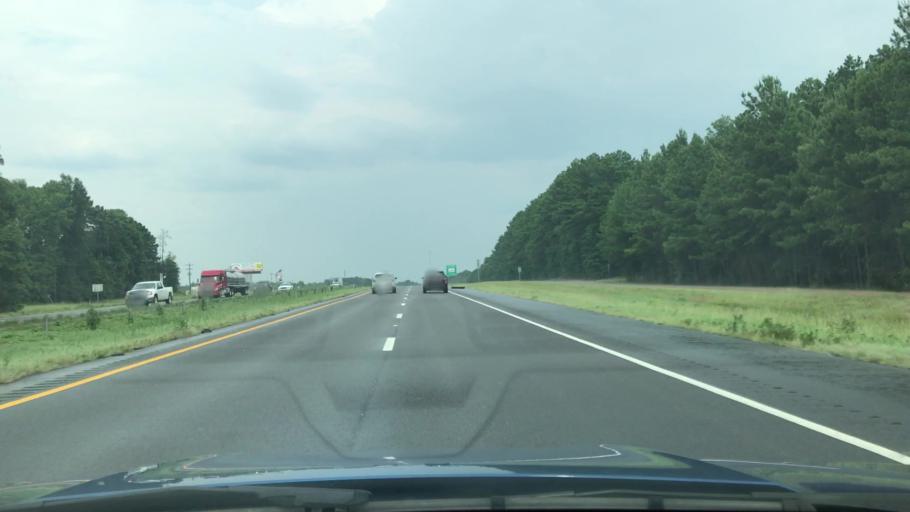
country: US
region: Texas
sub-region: Harrison County
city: Hallsville
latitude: 32.4858
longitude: -94.4839
